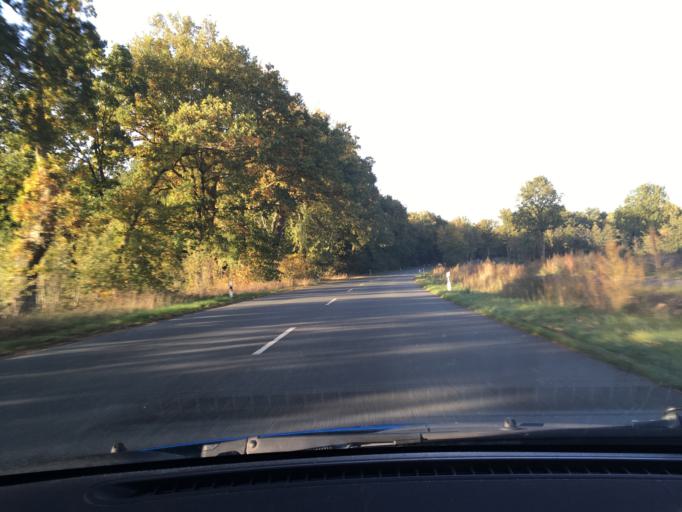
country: DE
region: Lower Saxony
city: Munster
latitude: 53.0124
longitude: 10.0488
